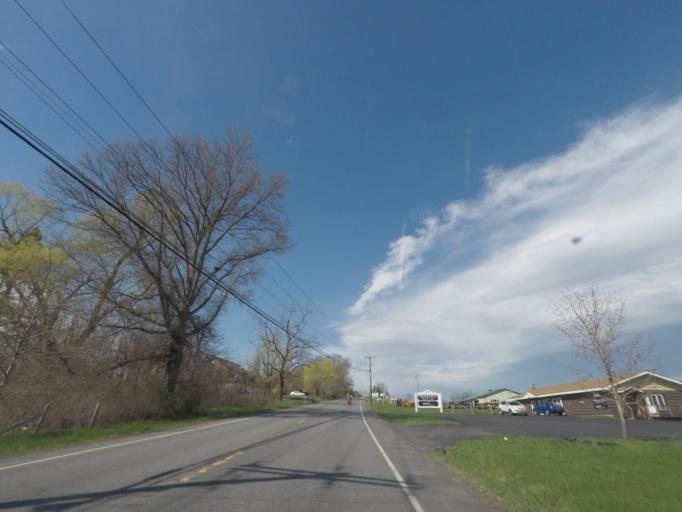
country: US
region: New York
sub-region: Greene County
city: Cairo
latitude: 42.4001
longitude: -74.0279
